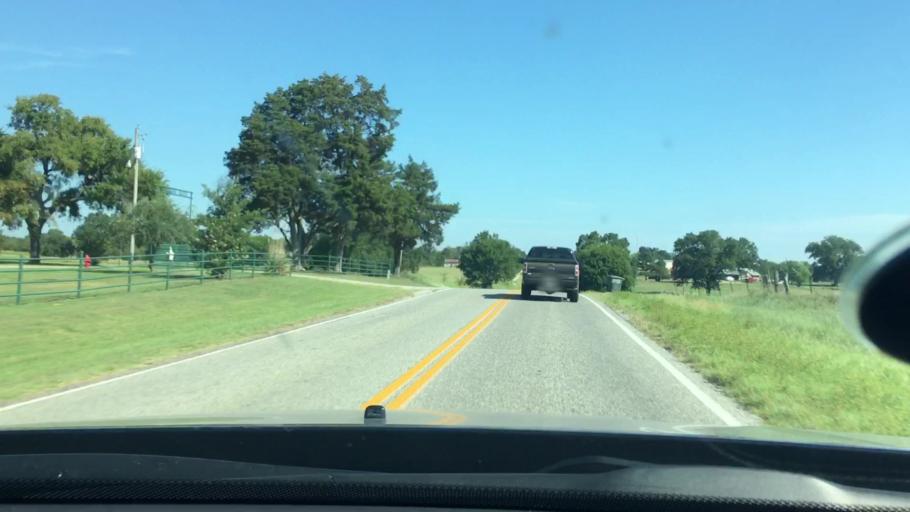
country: US
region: Oklahoma
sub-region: Johnston County
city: Tishomingo
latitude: 34.2702
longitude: -96.5487
